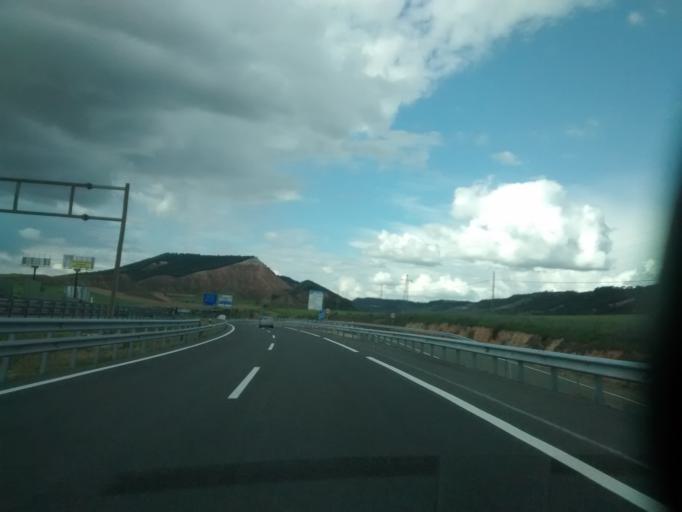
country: ES
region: Castille-La Mancha
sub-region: Provincia de Guadalajara
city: Guadalajara
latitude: 40.6523
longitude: -3.1250
